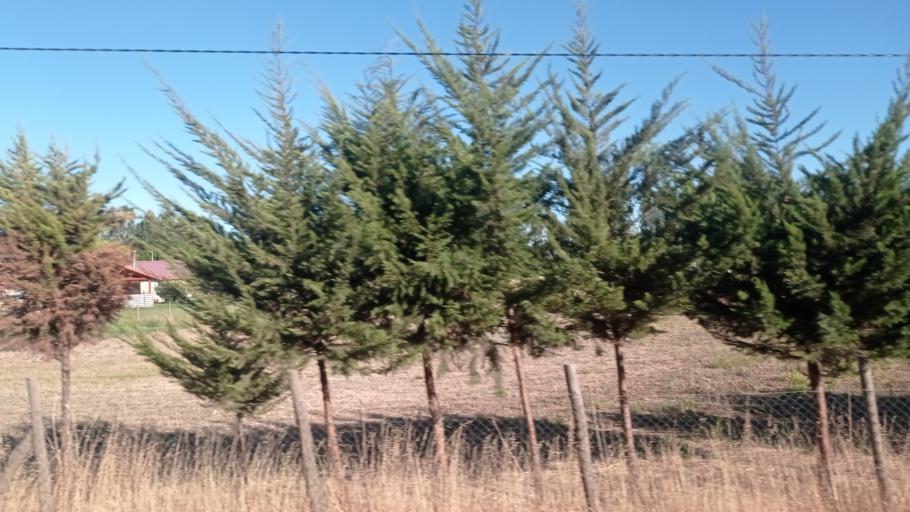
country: CL
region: Biobio
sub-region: Provincia de Biobio
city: Los Angeles
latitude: -37.5192
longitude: -72.5087
